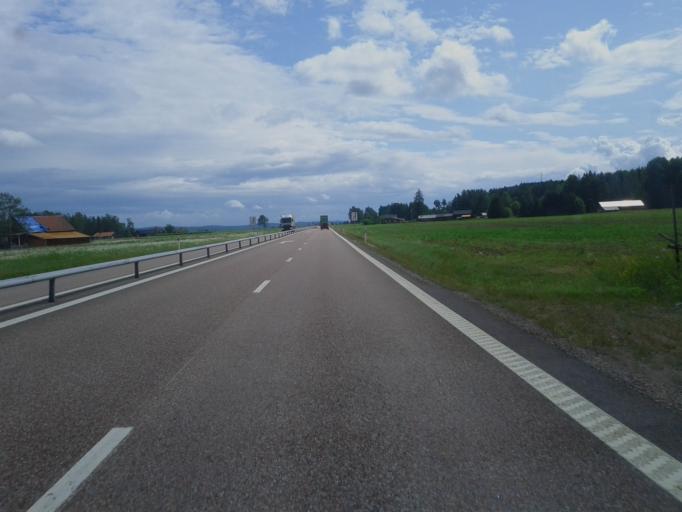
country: SE
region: Dalarna
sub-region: Hedemora Kommun
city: Hedemora
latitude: 60.3070
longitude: 15.9535
